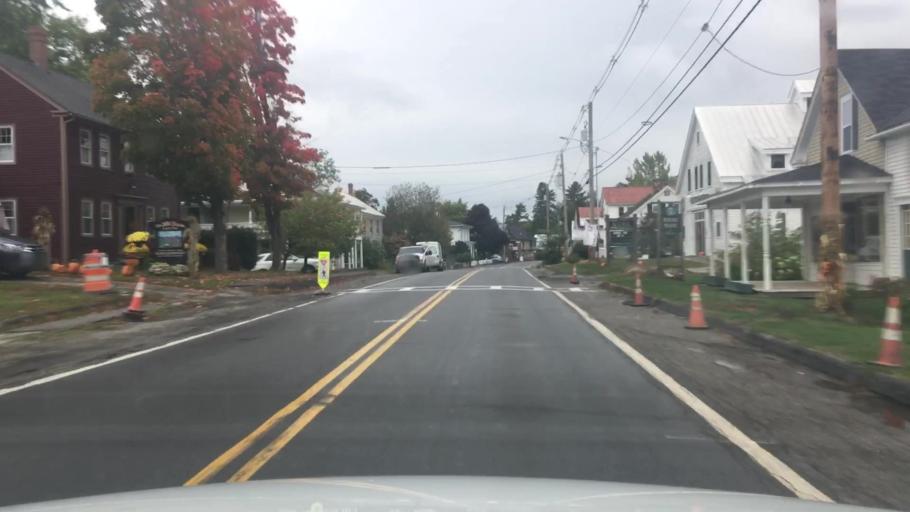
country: US
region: Maine
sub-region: Kennebec County
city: Rome
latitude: 44.5274
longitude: -69.8874
